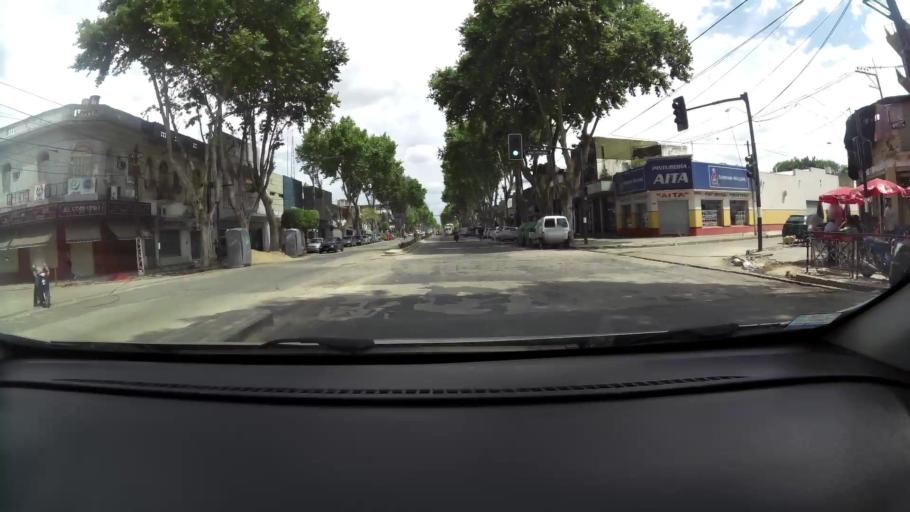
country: AR
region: Santa Fe
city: Gobernador Galvez
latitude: -32.9977
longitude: -60.6482
